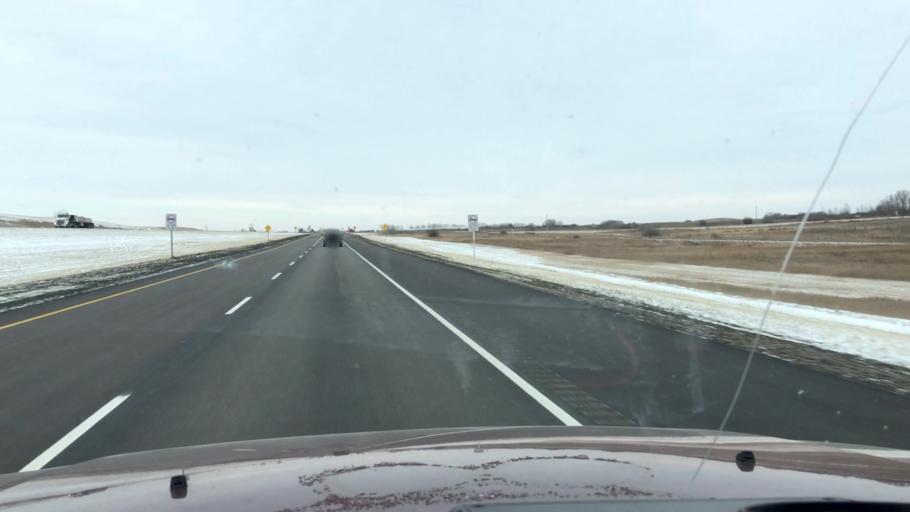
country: CA
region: Saskatchewan
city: Moose Jaw
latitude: 50.8659
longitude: -105.5978
